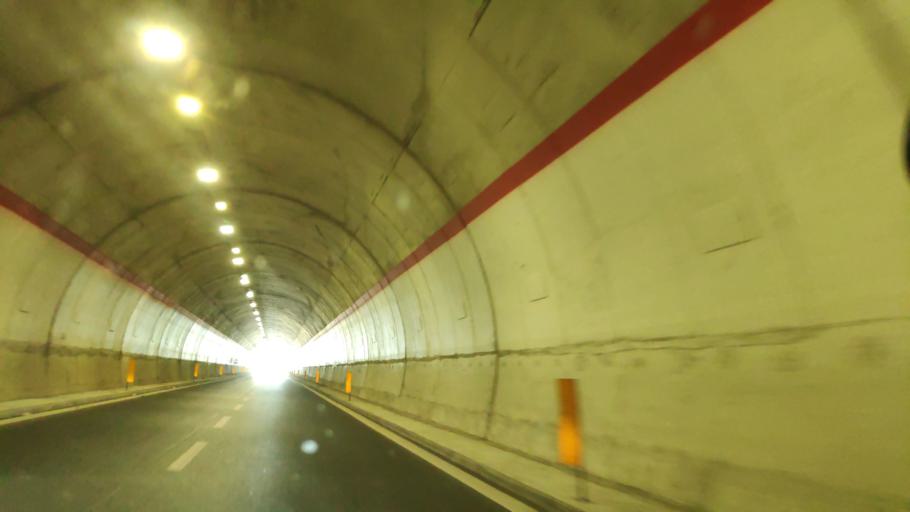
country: IT
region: Calabria
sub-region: Provincia di Reggio Calabria
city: Roccella Ionica
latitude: 38.3245
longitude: 16.3887
